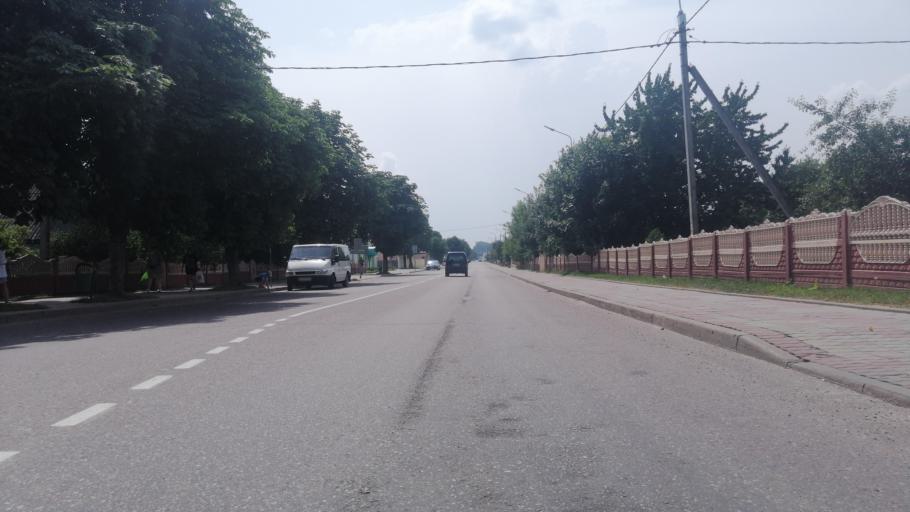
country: BY
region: Grodnenskaya
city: Navahrudak
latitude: 53.5913
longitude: 25.8173
